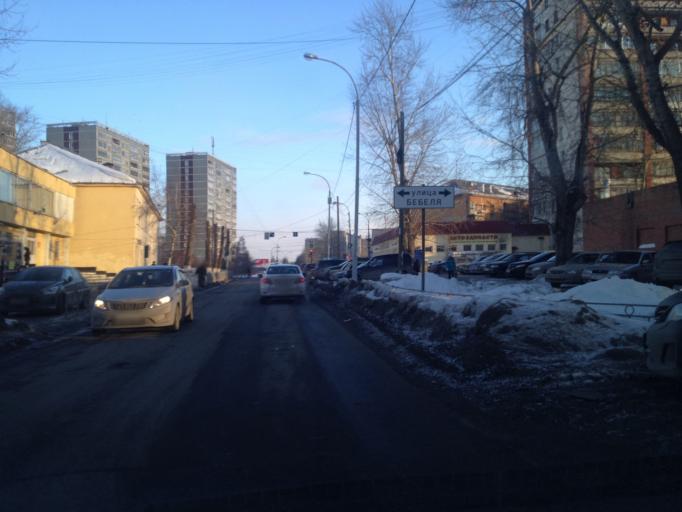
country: RU
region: Sverdlovsk
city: Yekaterinburg
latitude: 56.8718
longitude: 60.5476
